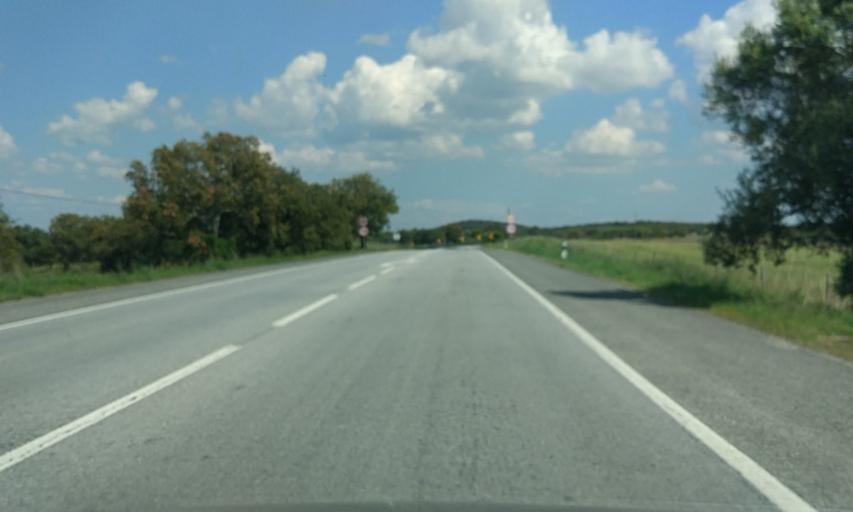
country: PT
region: Evora
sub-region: Montemor-O-Novo
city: Montemor-o-Novo
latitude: 38.6460
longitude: -8.3133
